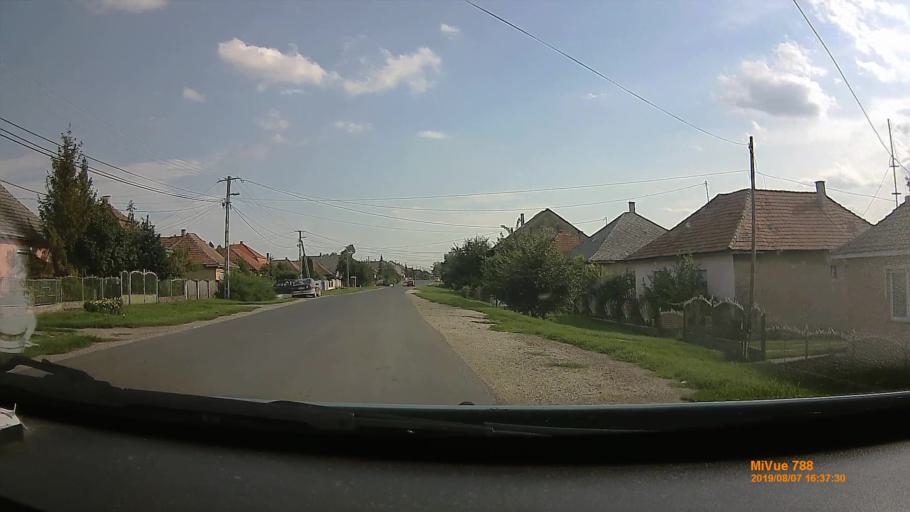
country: HU
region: Borsod-Abauj-Zemplen
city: Gonc
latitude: 48.4116
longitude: 21.2303
